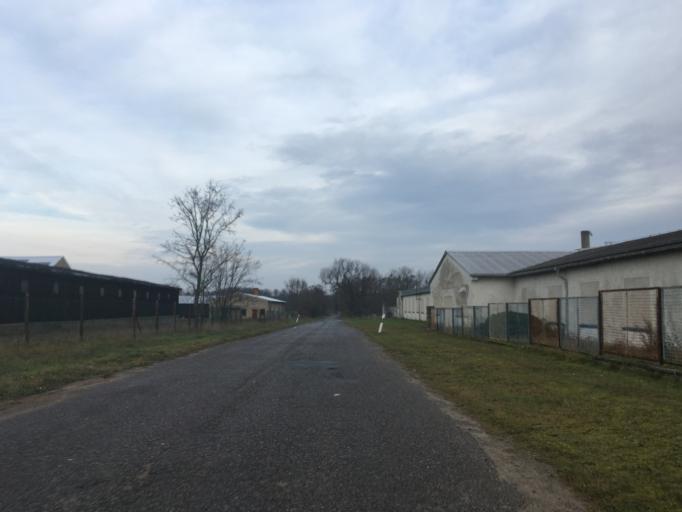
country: DE
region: Brandenburg
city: Seelow
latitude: 52.5627
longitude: 14.3480
